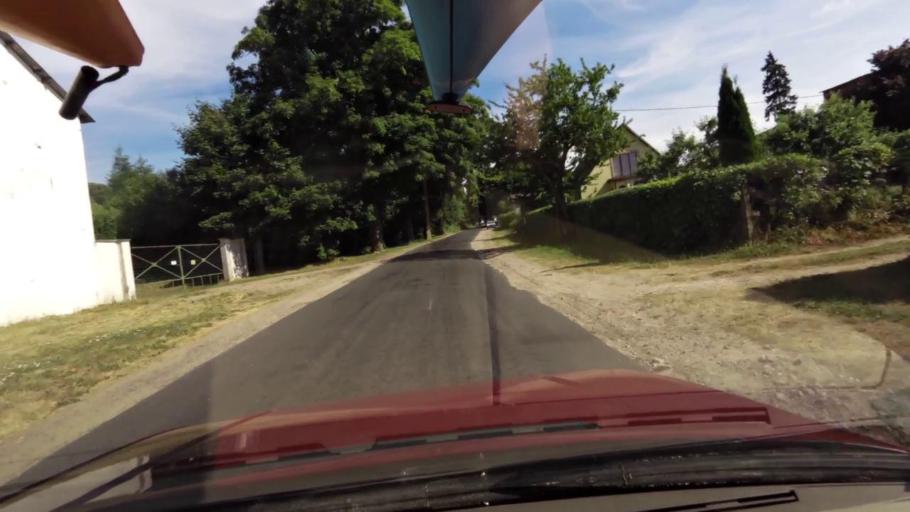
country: PL
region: Pomeranian Voivodeship
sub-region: Powiat bytowski
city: Miastko
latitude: 54.1193
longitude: 16.9470
